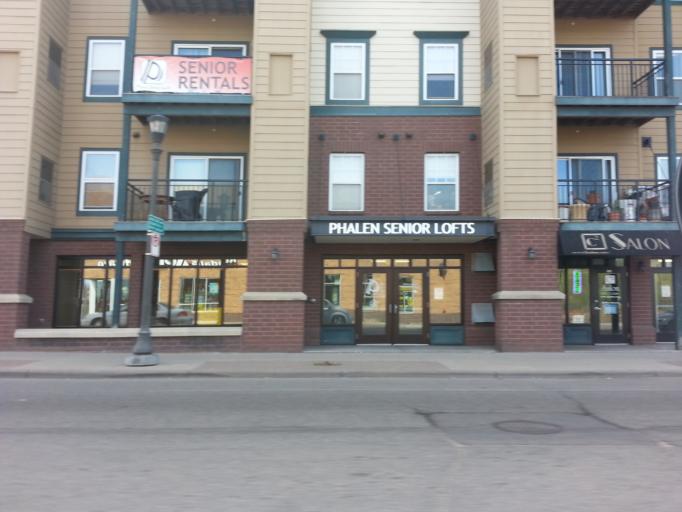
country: US
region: Minnesota
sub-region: Ramsey County
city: Saint Paul
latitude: 44.9663
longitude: -93.0735
